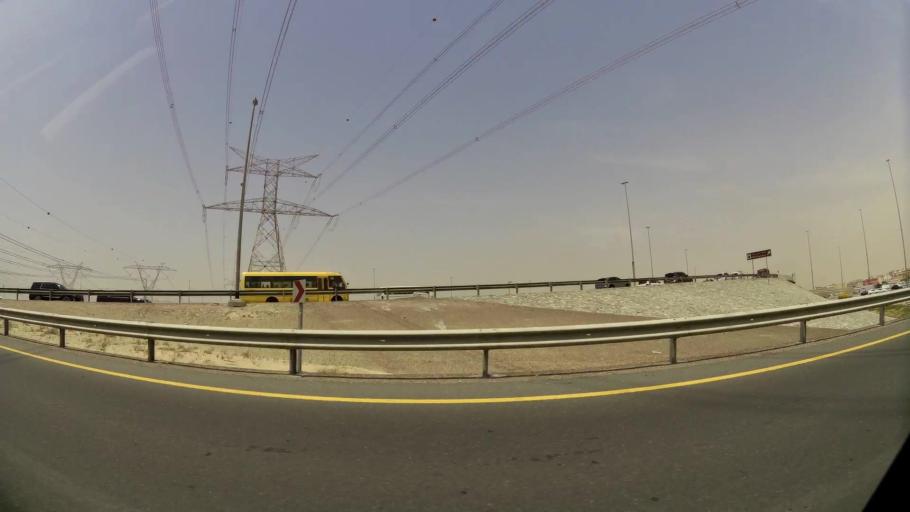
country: AE
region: Ash Shariqah
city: Sharjah
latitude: 25.2105
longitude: 55.4002
